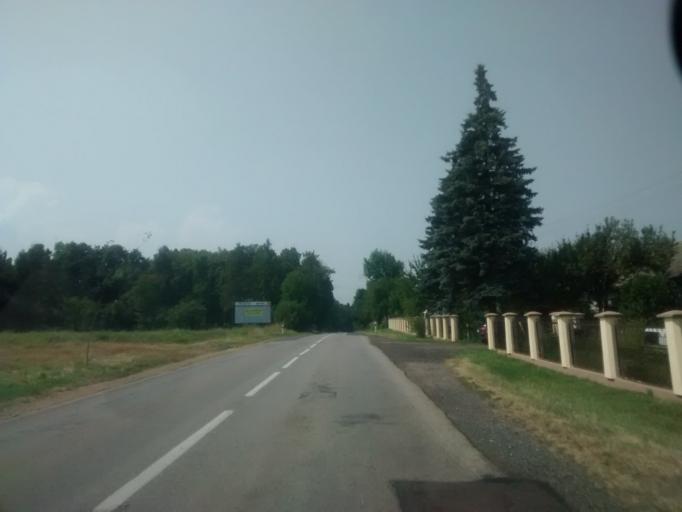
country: PL
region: Silesian Voivodeship
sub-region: Powiat czestochowski
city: Olsztyn
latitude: 50.7421
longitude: 19.3378
